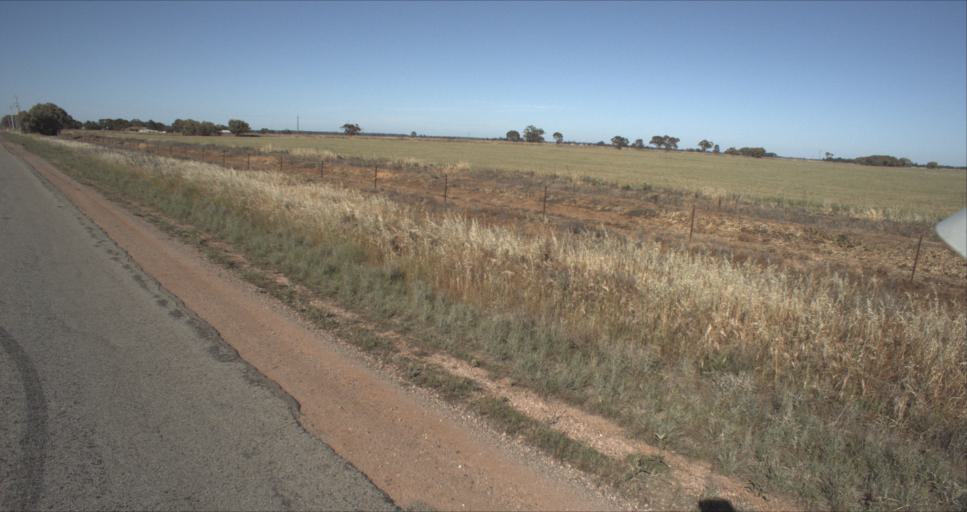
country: AU
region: New South Wales
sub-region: Leeton
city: Leeton
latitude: -34.5645
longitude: 146.3121
